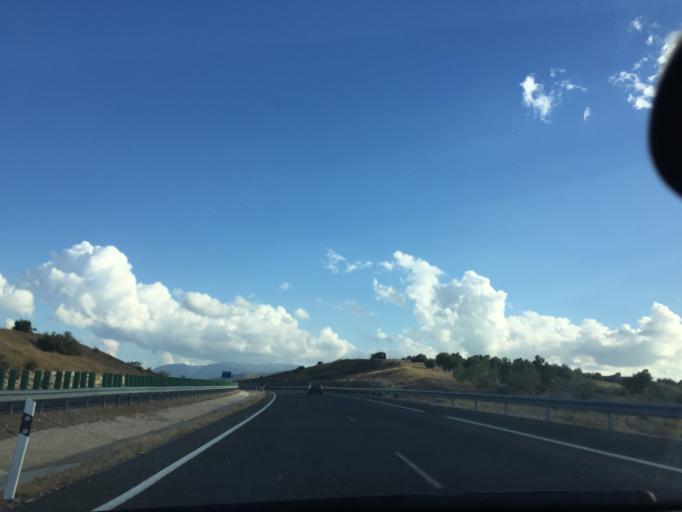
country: ES
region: Andalusia
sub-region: Provincia de Jaen
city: Jaen
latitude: 37.8099
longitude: -3.7347
